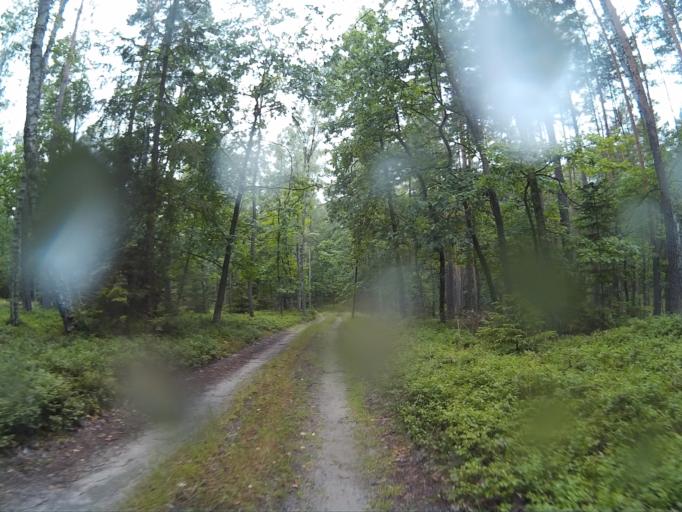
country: PL
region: Kujawsko-Pomorskie
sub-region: Powiat swiecki
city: Osie
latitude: 53.6574
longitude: 18.3739
